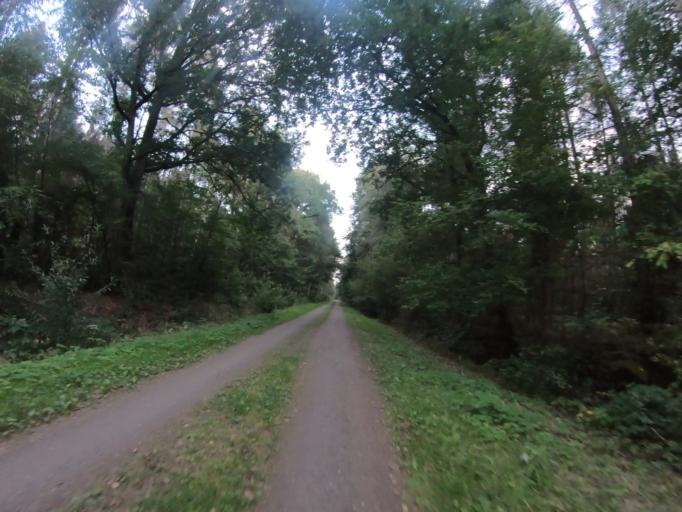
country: DE
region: Lower Saxony
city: Gifhorn
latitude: 52.5092
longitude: 10.5629
